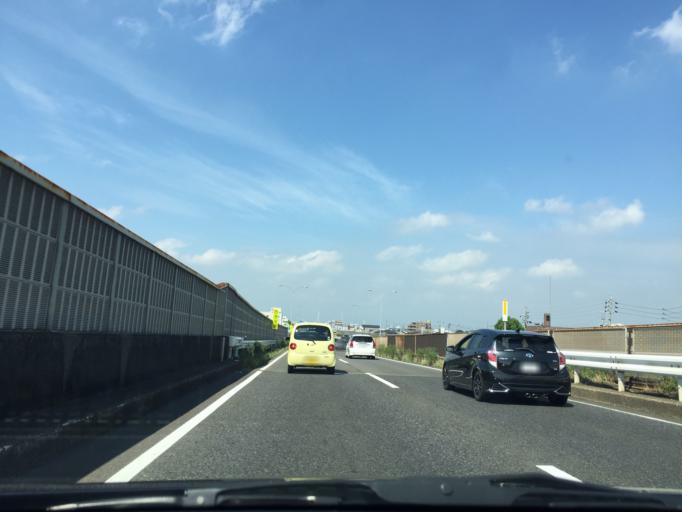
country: JP
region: Gifu
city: Kasamatsucho
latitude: 35.3879
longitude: 136.7631
